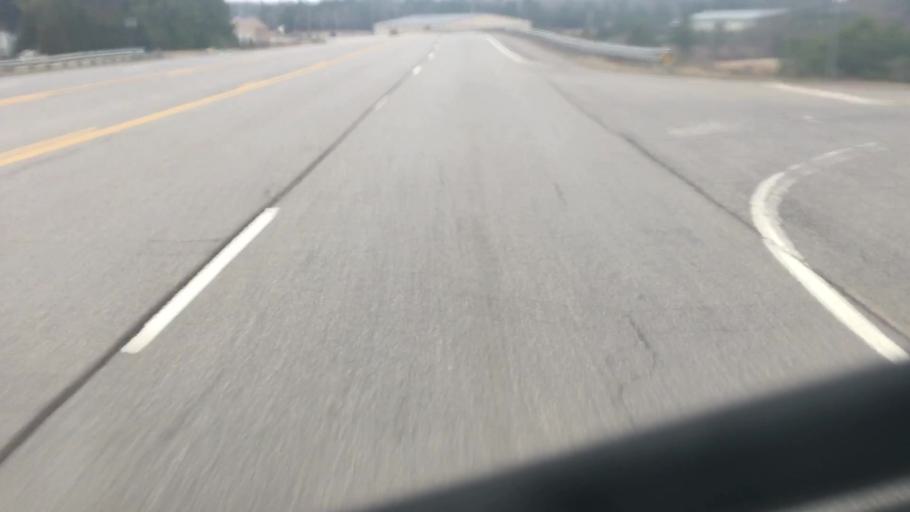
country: US
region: Alabama
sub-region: Walker County
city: Jasper
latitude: 33.8130
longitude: -87.2333
